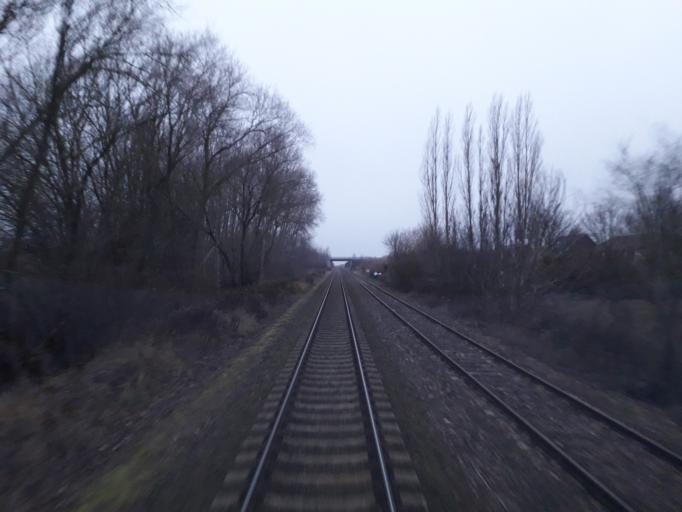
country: DE
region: Brandenburg
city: Pritzwalk
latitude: 53.1446
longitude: 12.1623
